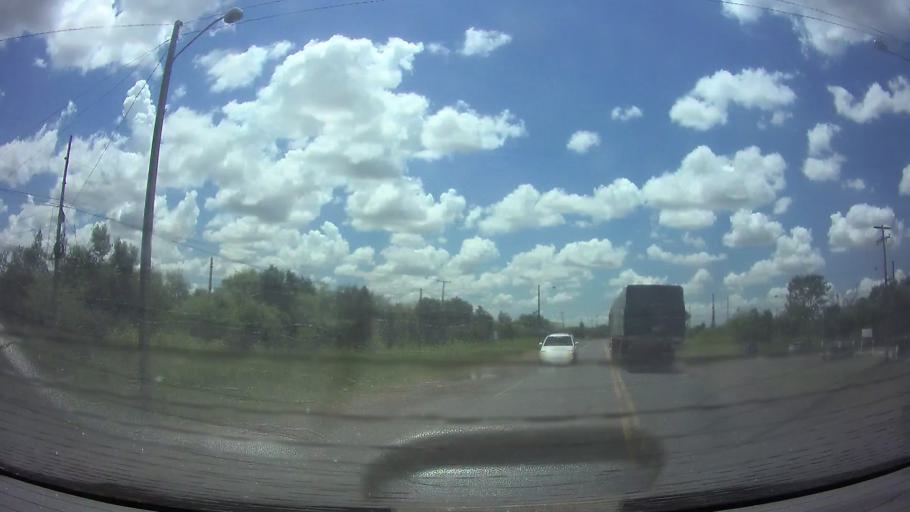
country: PY
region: Presidente Hayes
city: Nanawa
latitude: -25.2314
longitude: -57.6924
